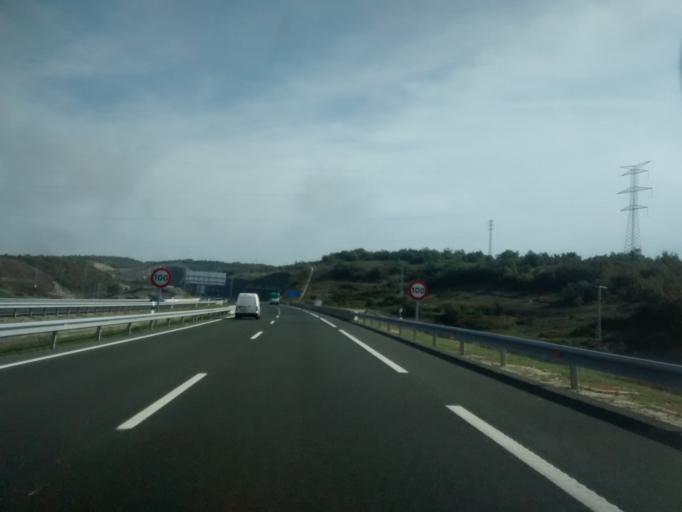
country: ES
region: Basque Country
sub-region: Provincia de Alava
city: Gasteiz / Vitoria
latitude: 42.9285
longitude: -2.6399
